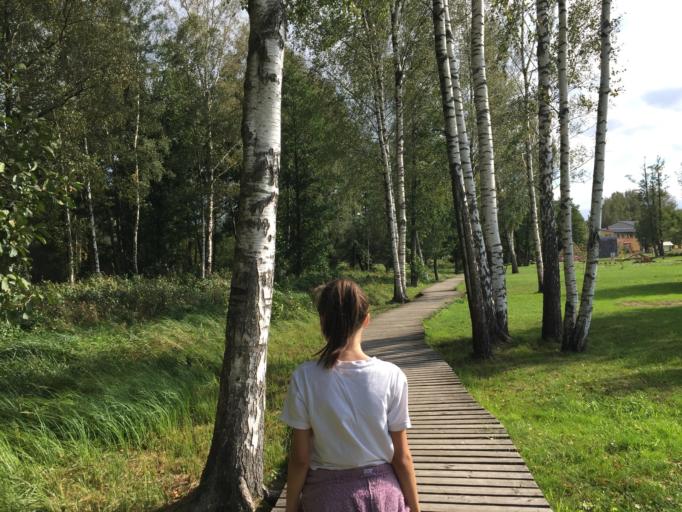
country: LV
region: Limbazu Rajons
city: Limbazi
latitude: 57.5040
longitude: 24.7028
